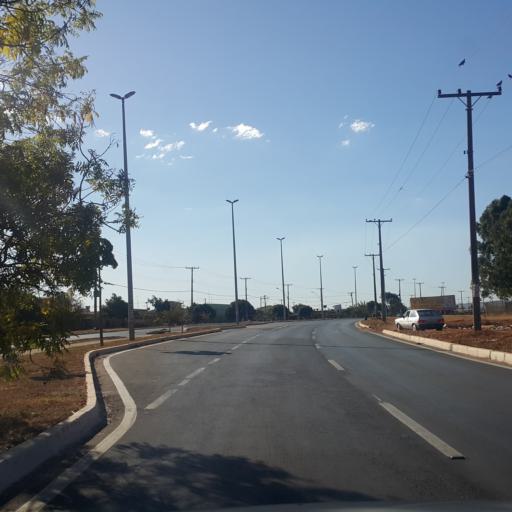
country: BR
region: Federal District
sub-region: Brasilia
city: Brasilia
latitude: -15.7948
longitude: -48.1174
